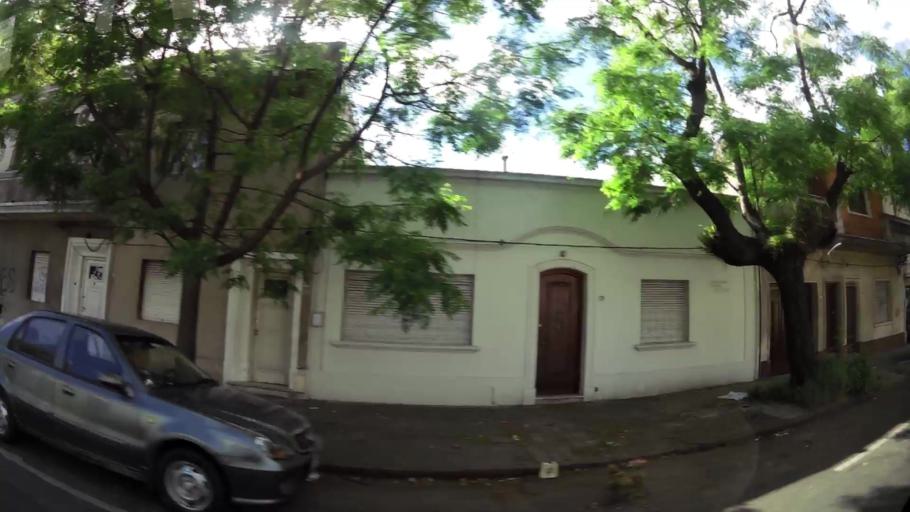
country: UY
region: Montevideo
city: Montevideo
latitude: -34.8782
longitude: -56.1755
